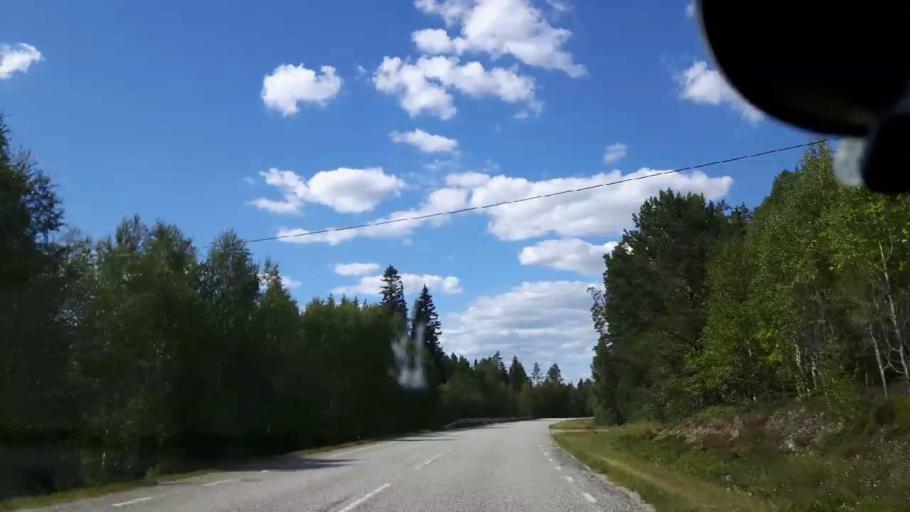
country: SE
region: Vaesternorrland
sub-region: Ange Kommun
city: Fransta
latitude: 62.7657
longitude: 16.2499
